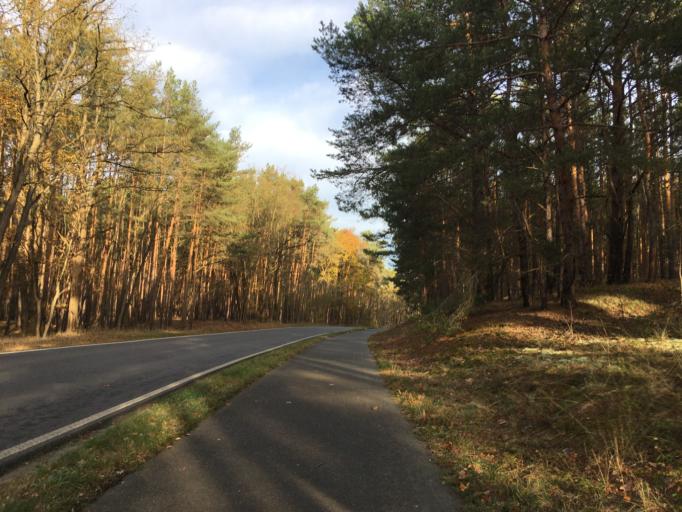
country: DE
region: Brandenburg
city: Luebben
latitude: 51.9550
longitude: 13.8819
